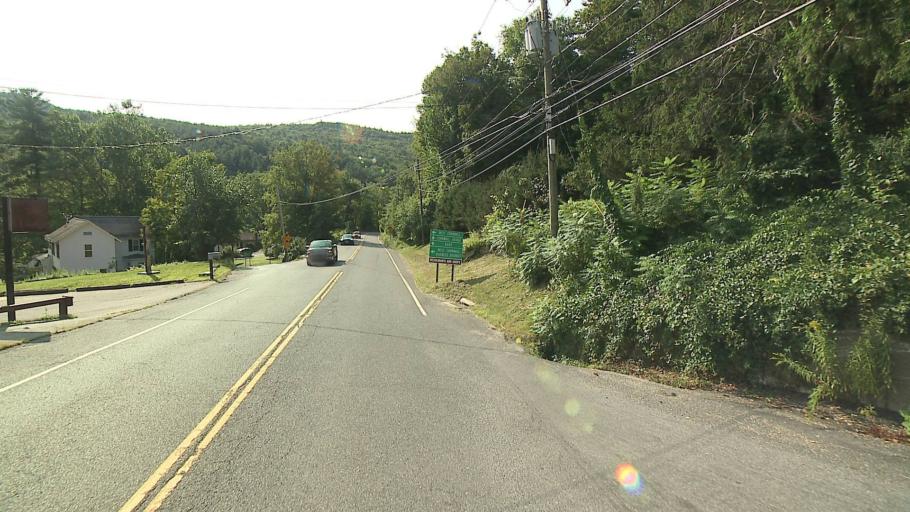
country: US
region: Connecticut
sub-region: Litchfield County
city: Canaan
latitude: 41.8720
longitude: -73.3654
